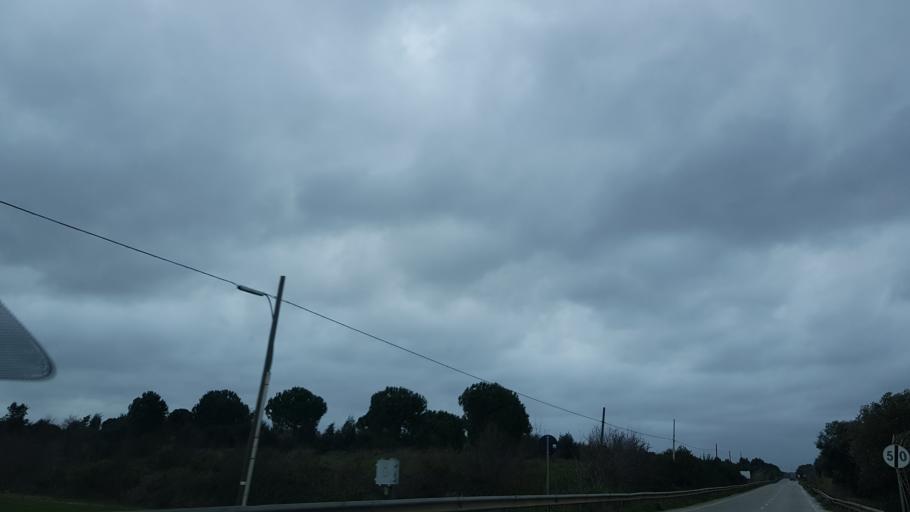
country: IT
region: Apulia
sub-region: Provincia di Brindisi
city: San Vito dei Normanni
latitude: 40.6532
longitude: 17.7888
